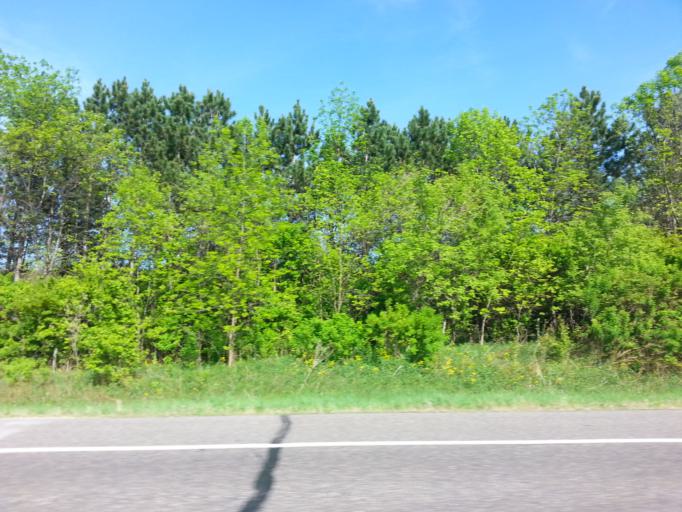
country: US
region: Minnesota
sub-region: Washington County
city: Oakdale
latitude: 44.9785
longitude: -92.9340
